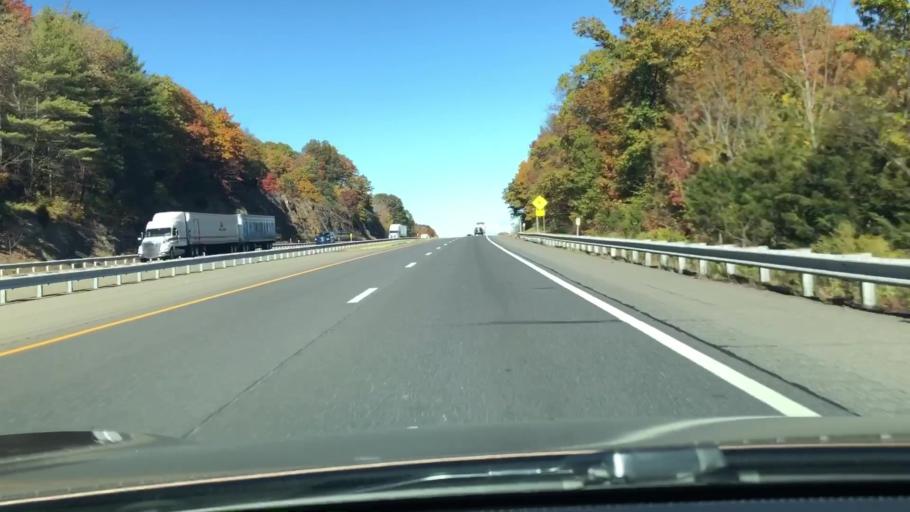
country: US
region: New York
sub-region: Ulster County
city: Lake Katrine
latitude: 41.9823
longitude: -74.0088
